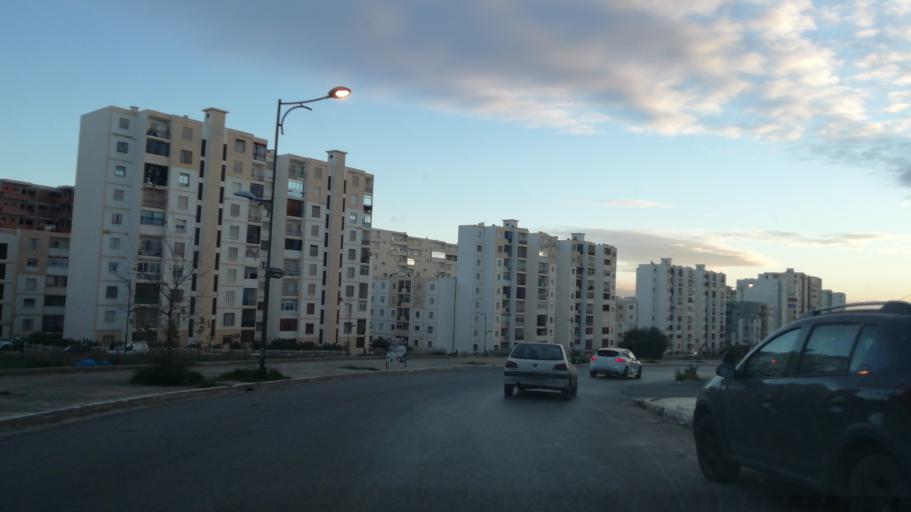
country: DZ
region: Oran
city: Bir el Djir
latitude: 35.7009
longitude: -0.5615
